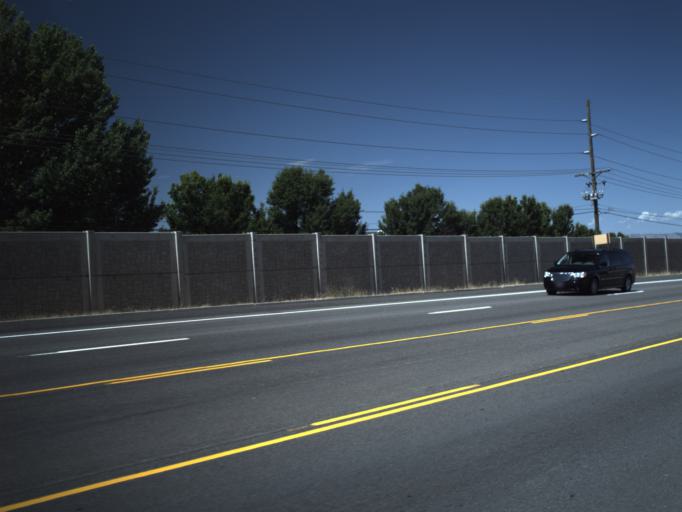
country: US
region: Utah
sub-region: Utah County
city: Spanish Fork
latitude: 40.1106
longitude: -111.6327
